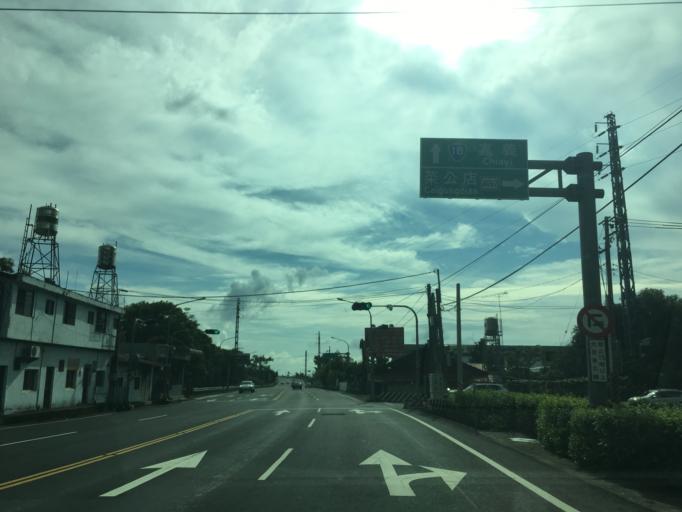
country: TW
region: Taiwan
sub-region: Chiayi
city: Jiayi Shi
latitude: 23.4532
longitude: 120.5572
